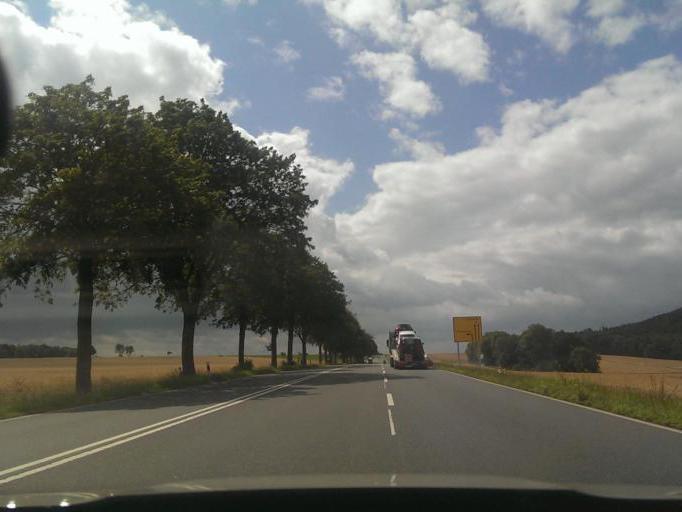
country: DE
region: Lower Saxony
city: Holenberg
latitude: 51.9153
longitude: 9.6140
